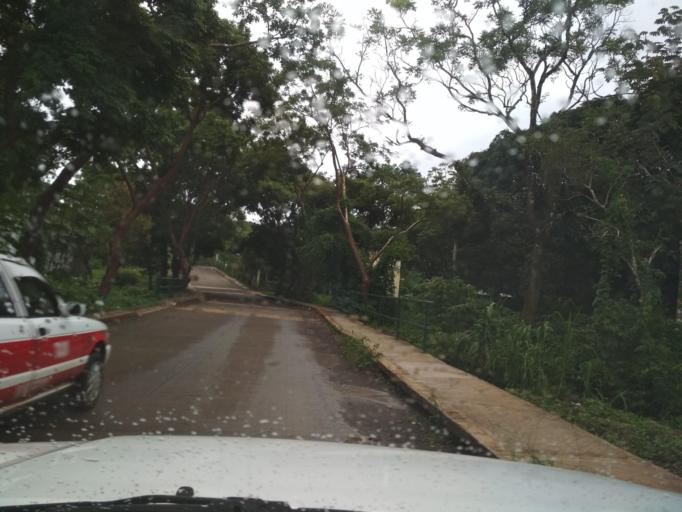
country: MX
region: Veracruz
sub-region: San Andres Tuxtla
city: Tonalapan
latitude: 18.4572
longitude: -95.2273
